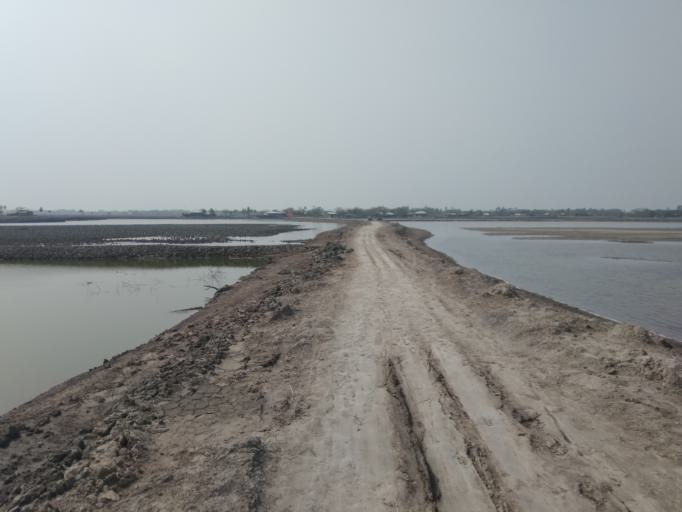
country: IN
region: West Bengal
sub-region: North 24 Parganas
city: Taki
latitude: 22.3467
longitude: 89.2262
